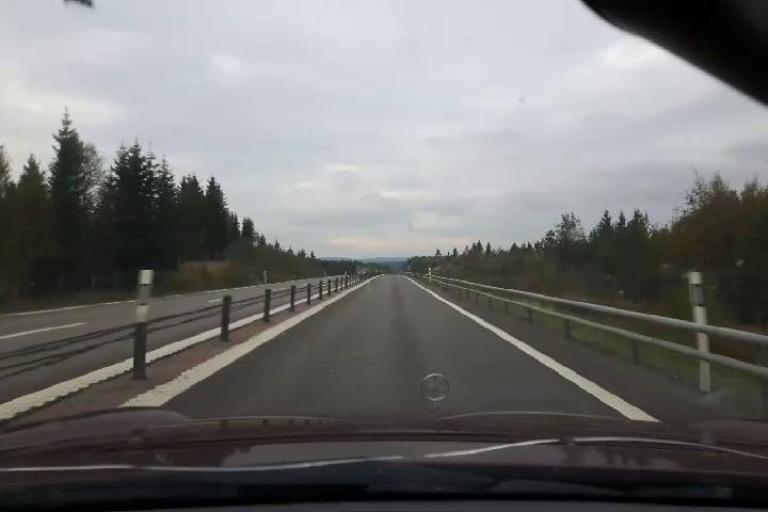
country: SE
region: Vaesternorrland
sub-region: Haernoesands Kommun
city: Haernoesand
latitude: 62.7163
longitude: 17.9096
